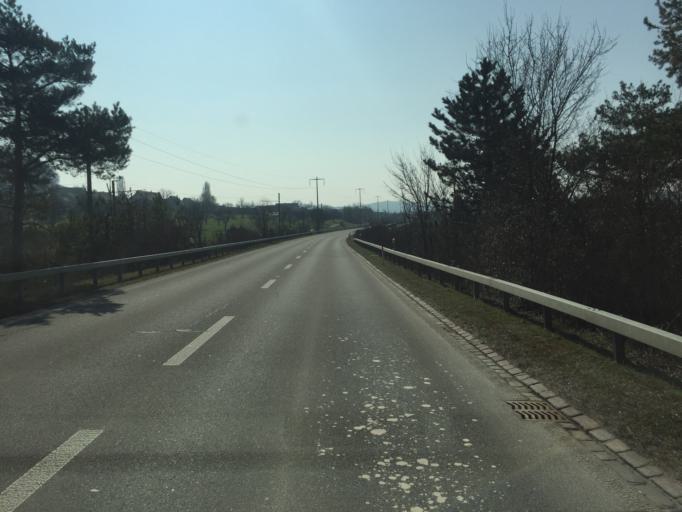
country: CH
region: Thurgau
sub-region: Frauenfeld District
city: Diessenhofen
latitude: 47.6447
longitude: 8.7864
